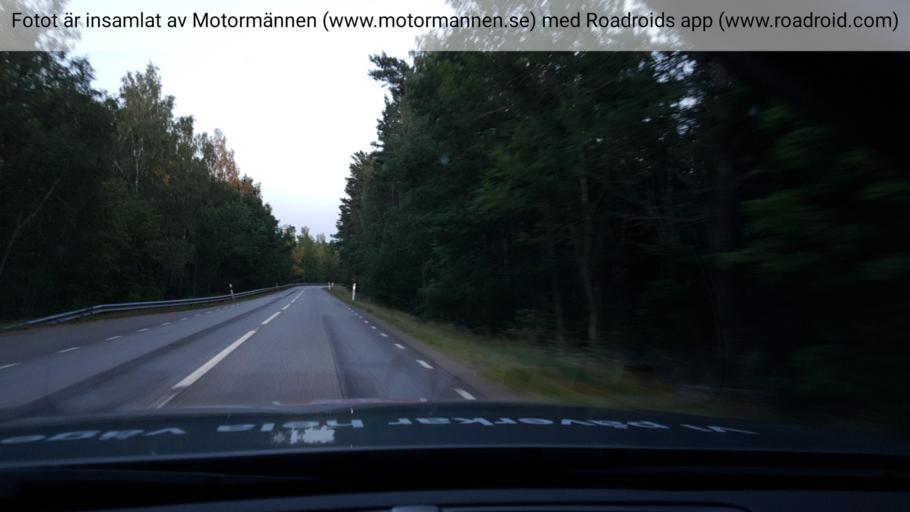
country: SE
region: Vaestmanland
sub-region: Hallstahammars Kommun
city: Hallstahammar
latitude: 59.6560
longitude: 16.1836
